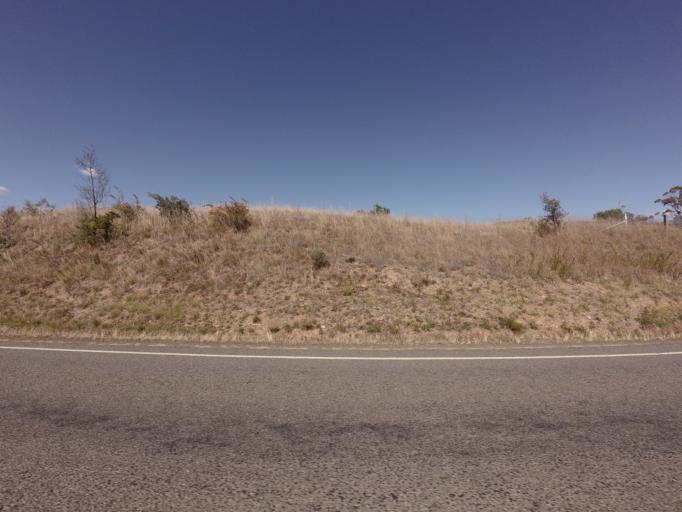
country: AU
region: Tasmania
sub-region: Northern Midlands
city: Evandale
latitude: -41.7456
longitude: 147.7843
